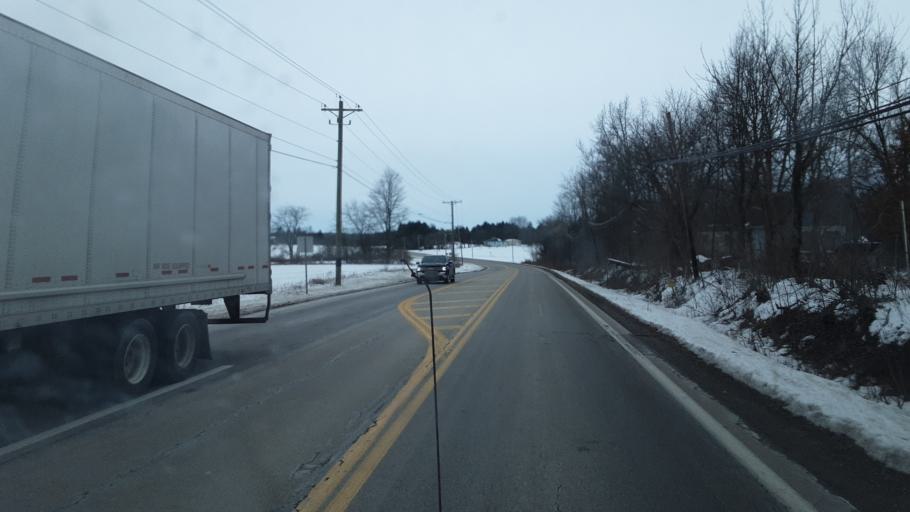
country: US
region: Ohio
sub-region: Union County
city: New California
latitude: 40.1492
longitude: -83.2436
